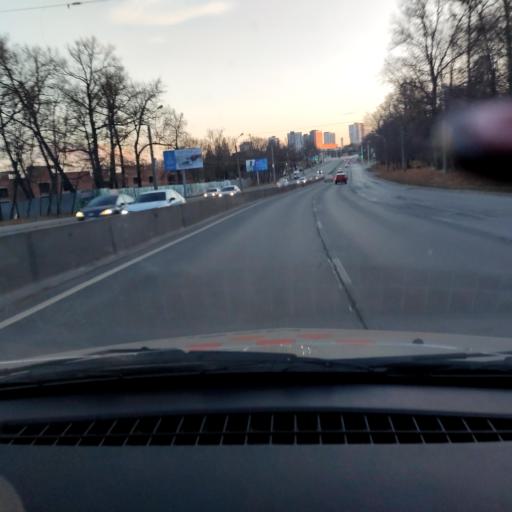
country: RU
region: Bashkortostan
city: Ufa
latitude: 54.7339
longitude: 56.0262
